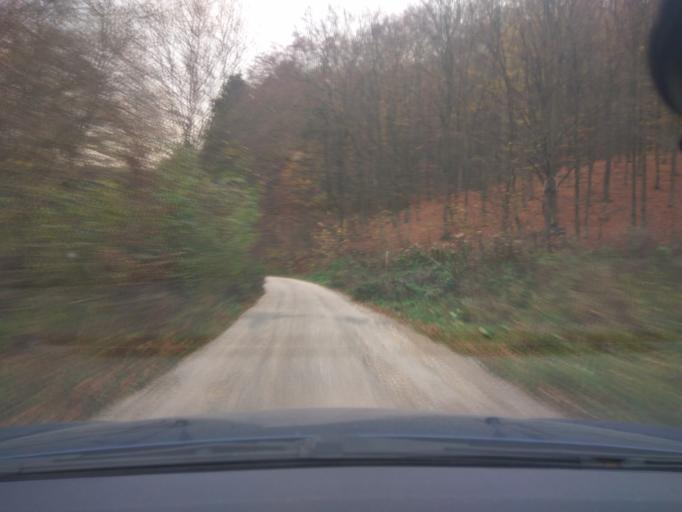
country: SK
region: Trnavsky
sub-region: Okres Trnava
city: Piestany
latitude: 48.6040
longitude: 17.9305
